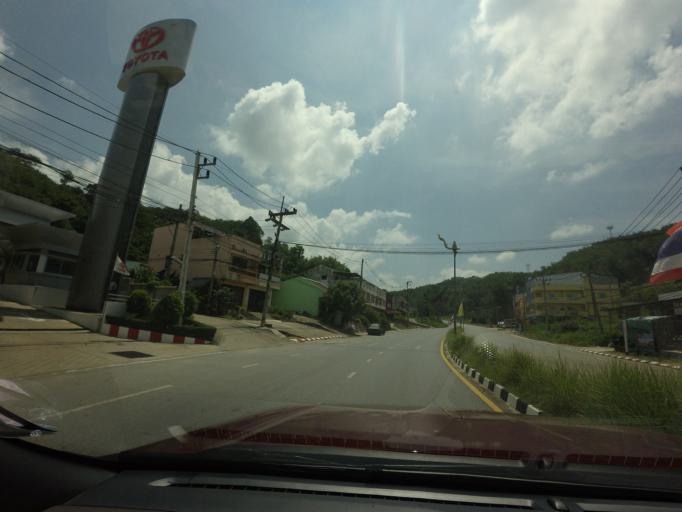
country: TH
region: Yala
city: Betong
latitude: 5.7886
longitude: 101.0720
